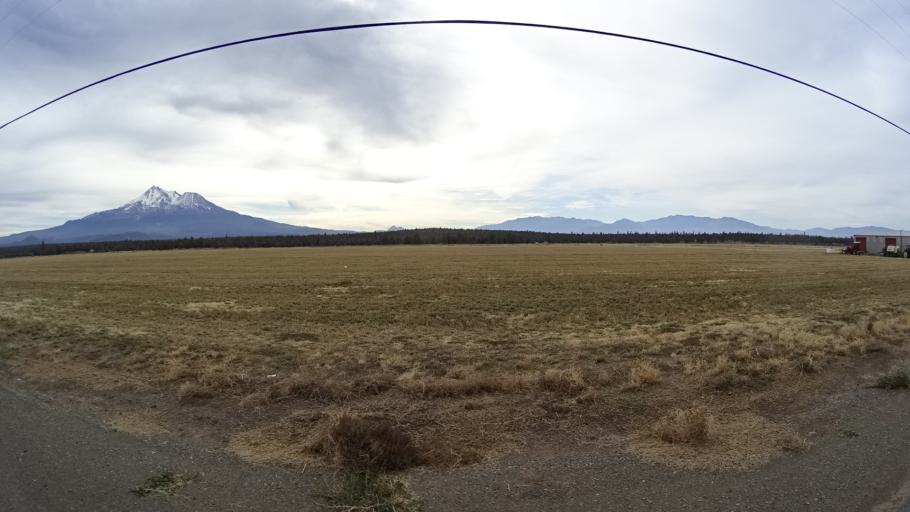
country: US
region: California
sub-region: Siskiyou County
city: Weed
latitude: 41.5954
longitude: -122.3294
